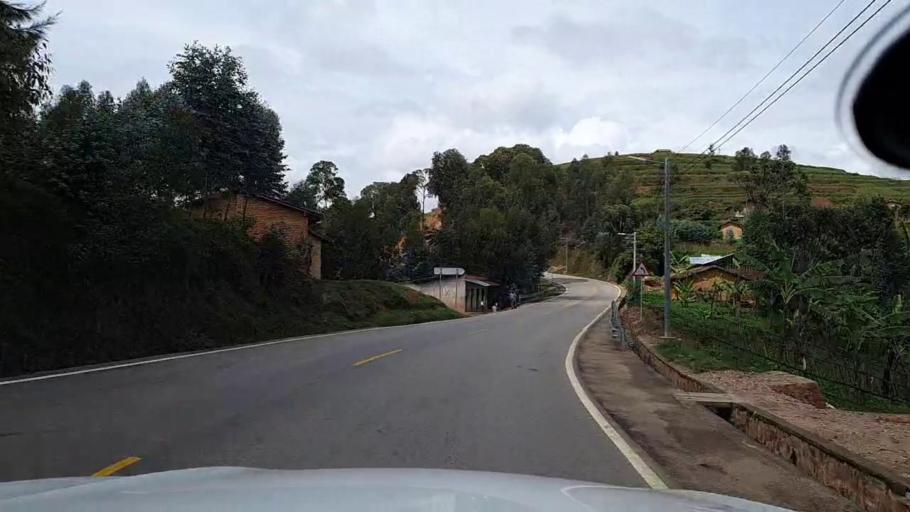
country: RW
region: Southern Province
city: Nzega
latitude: -2.5200
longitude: 29.4568
